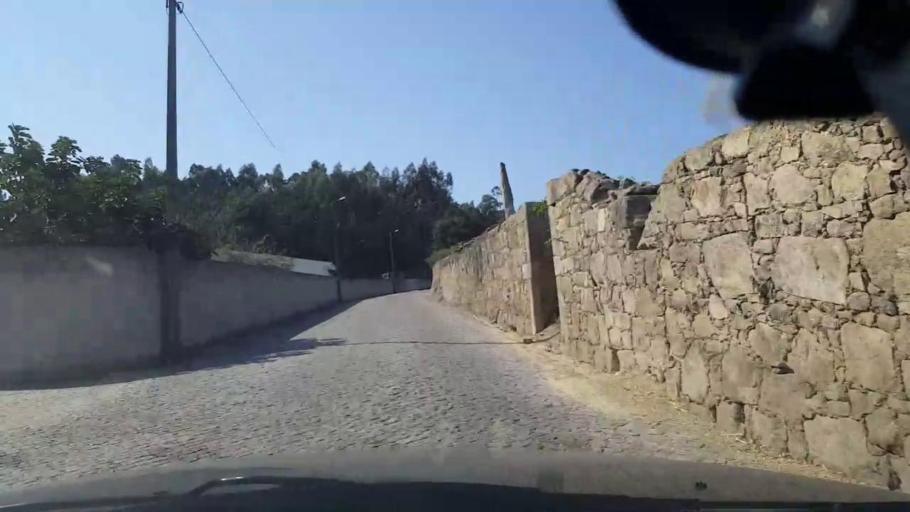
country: PT
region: Porto
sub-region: Povoa de Varzim
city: Pedroso
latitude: 41.4017
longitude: -8.6936
